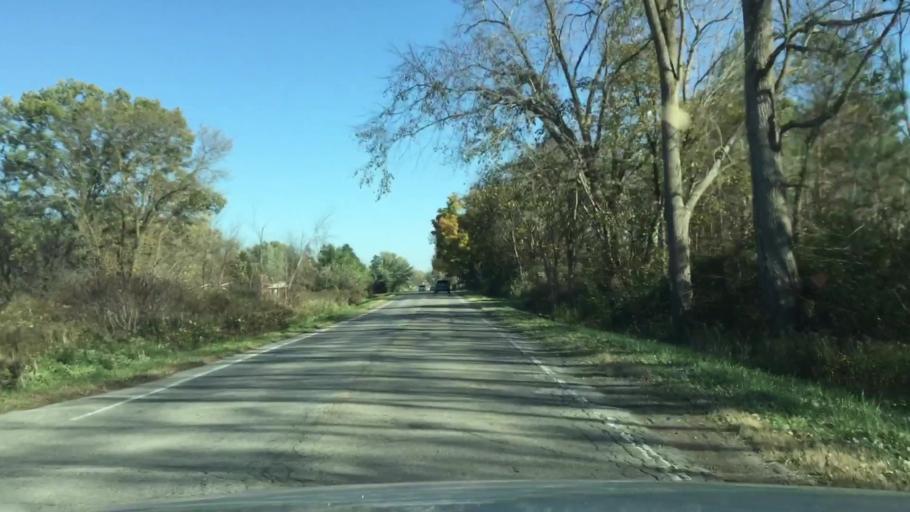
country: US
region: Michigan
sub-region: Lapeer County
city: Lapeer
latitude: 43.0721
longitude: -83.3371
